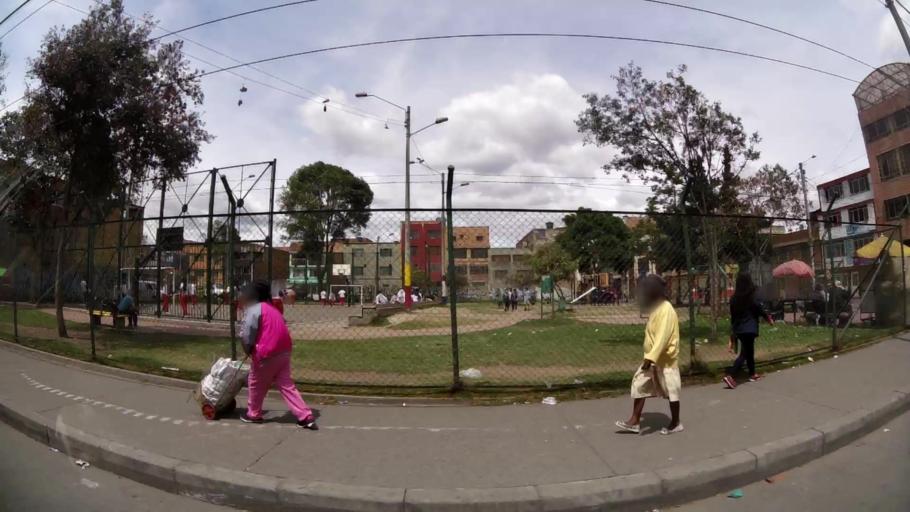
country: CO
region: Cundinamarca
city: Soacha
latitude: 4.6379
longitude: -74.1666
